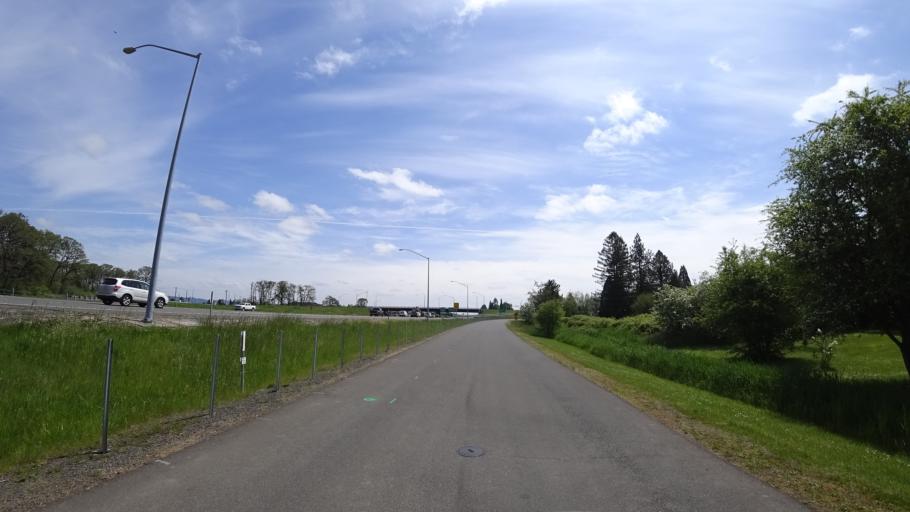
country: US
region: Oregon
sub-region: Washington County
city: Rockcreek
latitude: 45.5651
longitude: -122.9301
